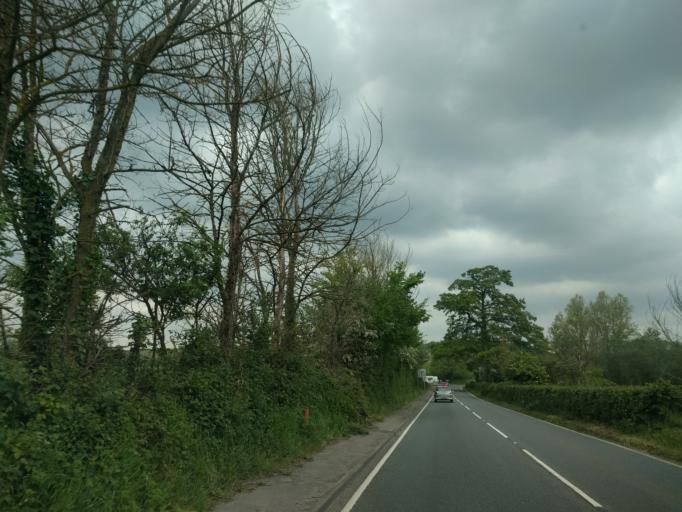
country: GB
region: England
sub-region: Somerset
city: Ilchester
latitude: 51.0566
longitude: -2.7211
